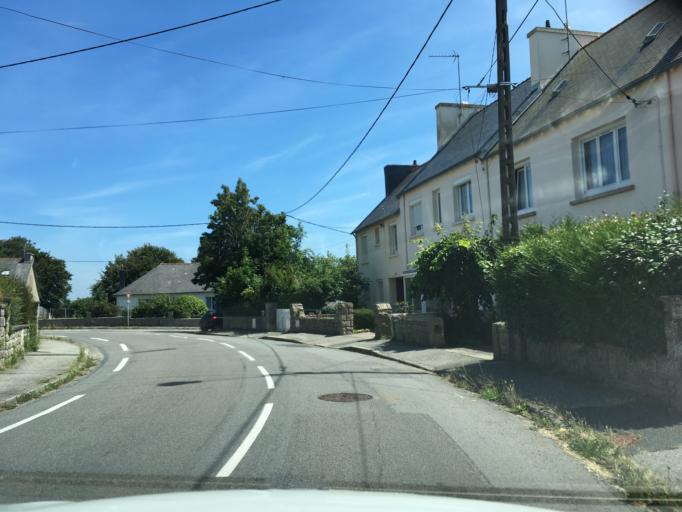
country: FR
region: Brittany
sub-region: Departement du Finistere
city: Quimper
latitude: 47.9965
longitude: -4.1261
